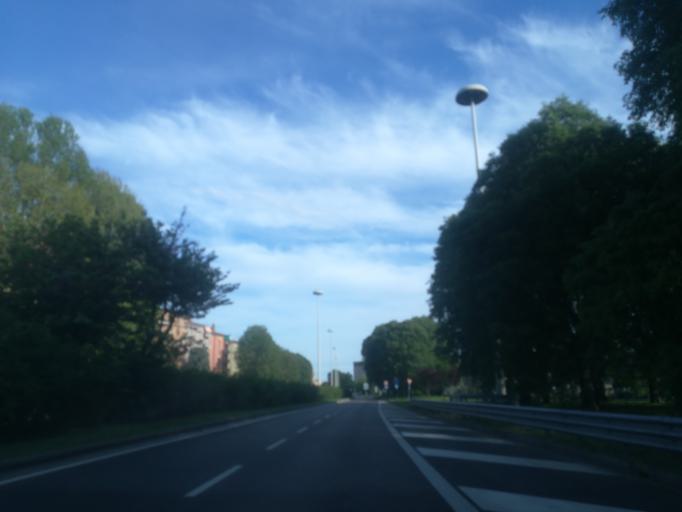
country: IT
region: Lombardy
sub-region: Citta metropolitana di Milano
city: Bresso
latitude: 45.5049
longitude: 9.1845
